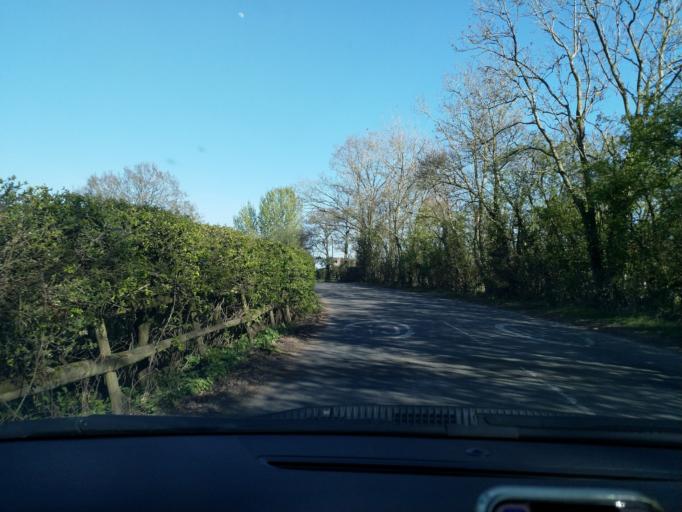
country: GB
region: England
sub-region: Warwickshire
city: Warwick
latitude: 52.2802
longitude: -1.6293
